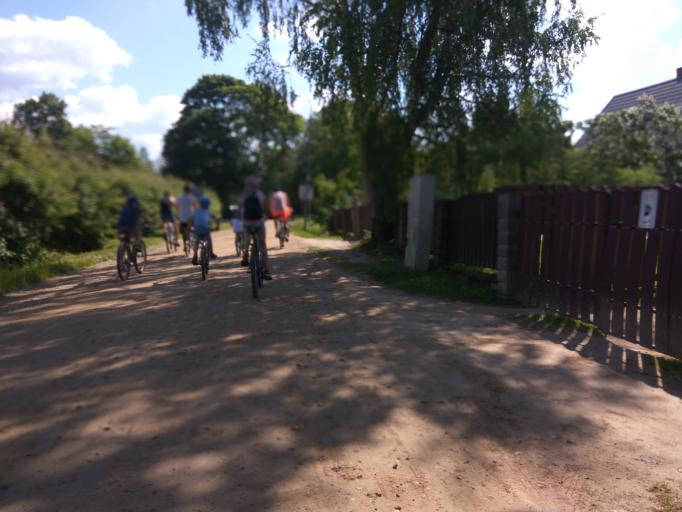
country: LV
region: Kuldigas Rajons
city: Kuldiga
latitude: 56.9581
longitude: 21.9725
